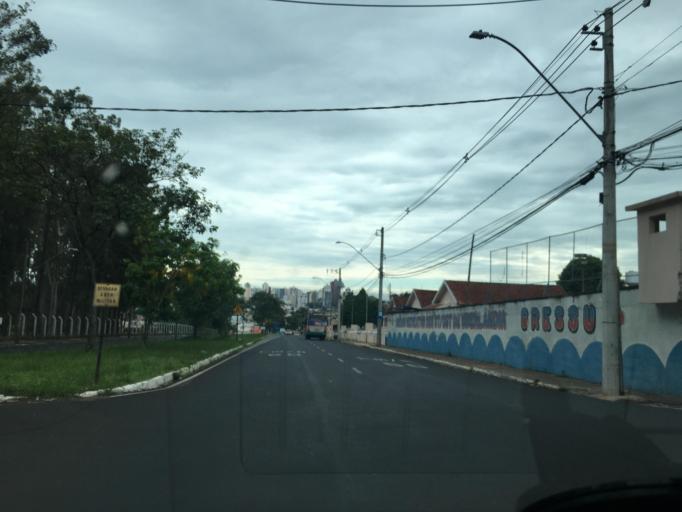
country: BR
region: Minas Gerais
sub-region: Uberlandia
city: Uberlandia
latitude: -18.9268
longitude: -48.3060
